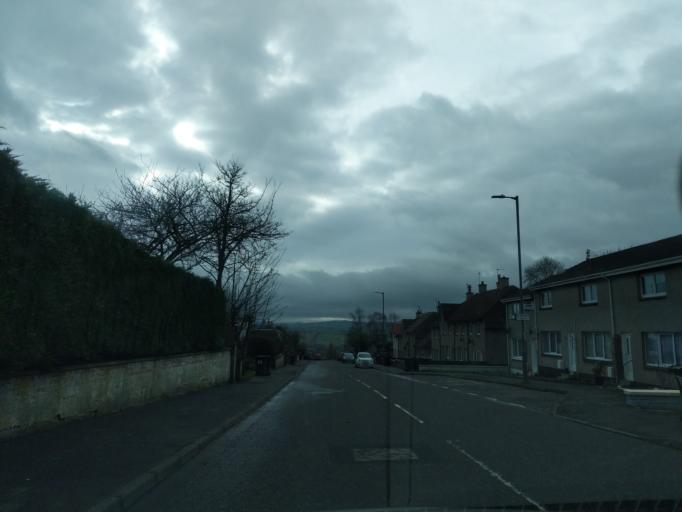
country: GB
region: Scotland
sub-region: South Lanarkshire
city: Carluke
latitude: 55.7113
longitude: -3.8422
